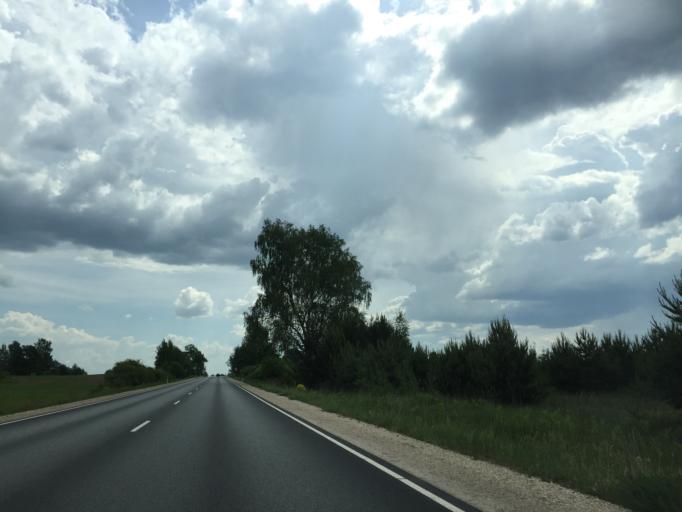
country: LV
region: Ikskile
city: Ikskile
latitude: 56.8724
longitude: 24.5375
